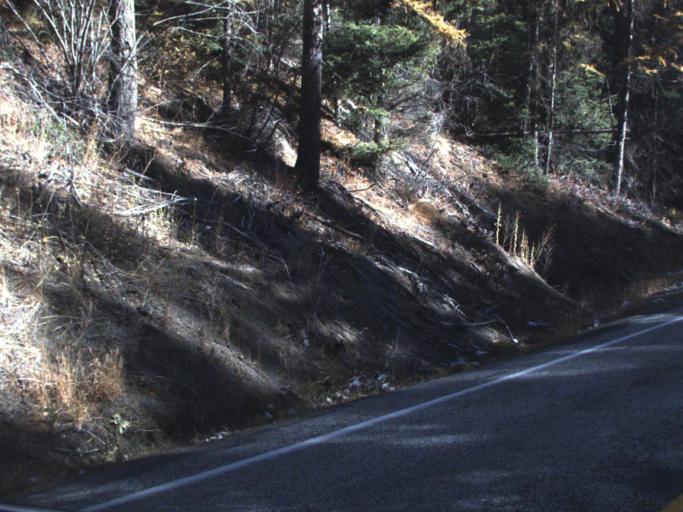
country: US
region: Washington
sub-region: Ferry County
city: Republic
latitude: 48.6220
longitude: -118.4078
